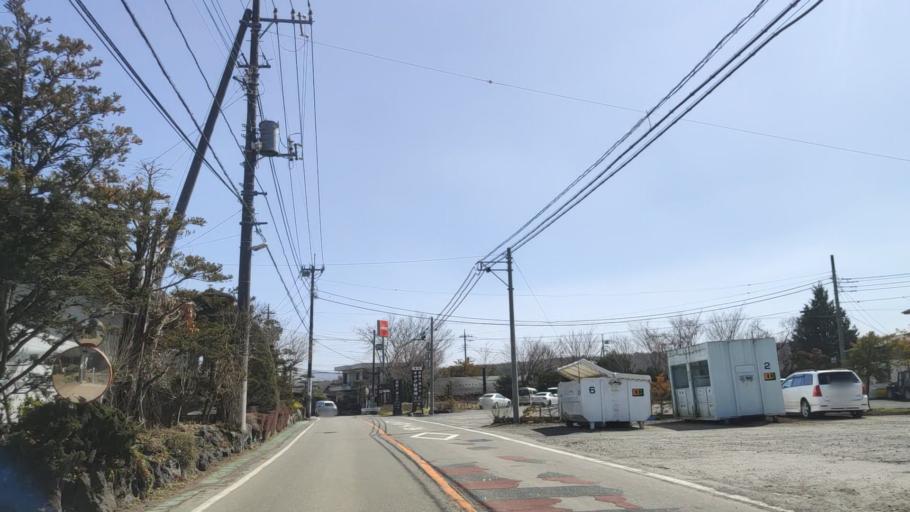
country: JP
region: Yamanashi
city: Fujikawaguchiko
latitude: 35.4608
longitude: 138.8355
